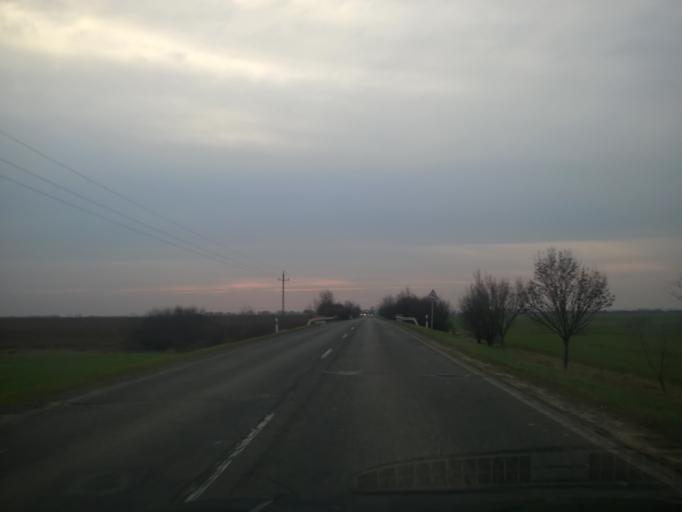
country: HU
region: Baranya
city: Szentlorinc
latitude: 46.0457
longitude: 17.9099
